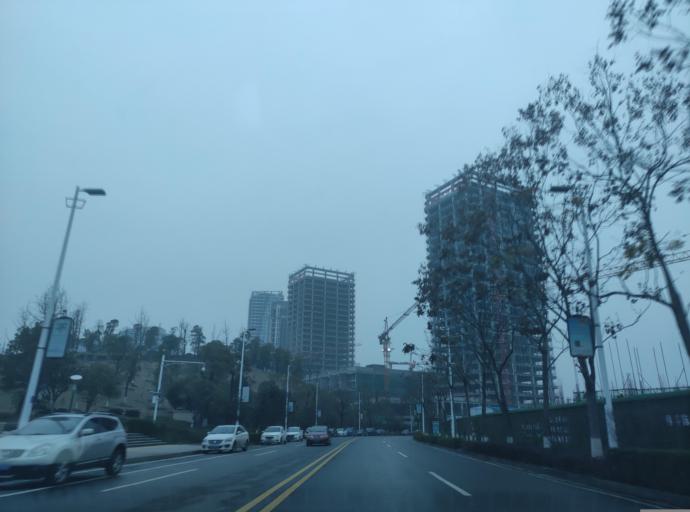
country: CN
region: Jiangxi Sheng
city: Pingxiang
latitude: 27.6651
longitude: 113.8828
